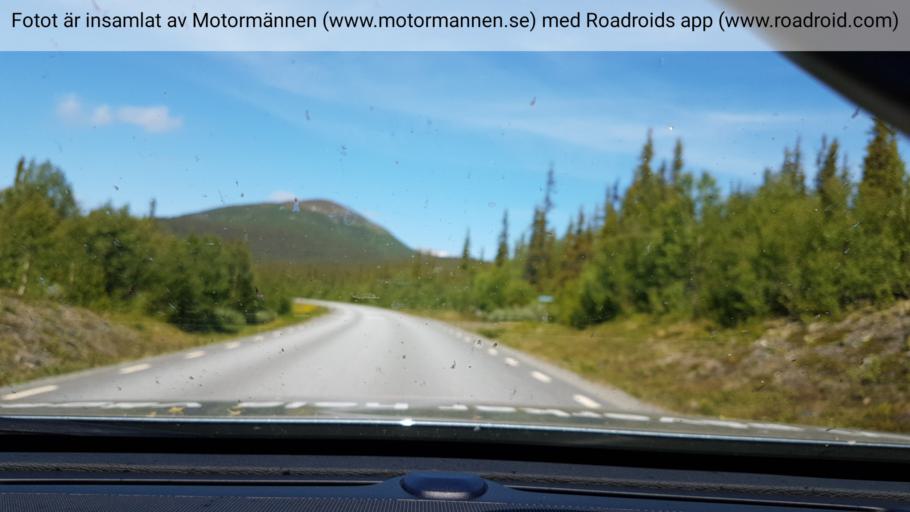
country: SE
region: Vaesterbotten
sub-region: Vilhelmina Kommun
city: Sjoberg
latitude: 64.8053
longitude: 15.2745
